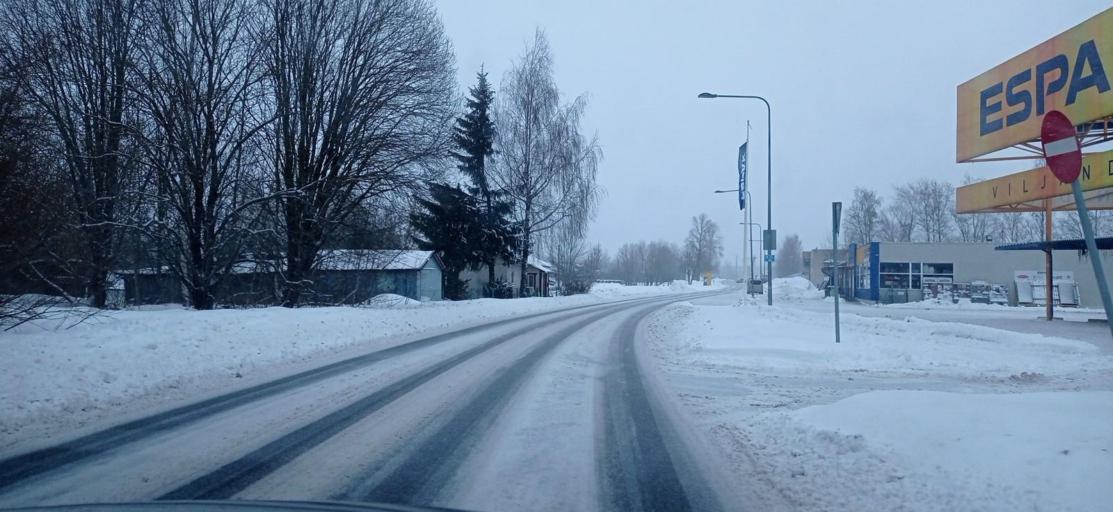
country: EE
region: Viljandimaa
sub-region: Viljandi linn
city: Viljandi
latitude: 58.3513
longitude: 25.5693
